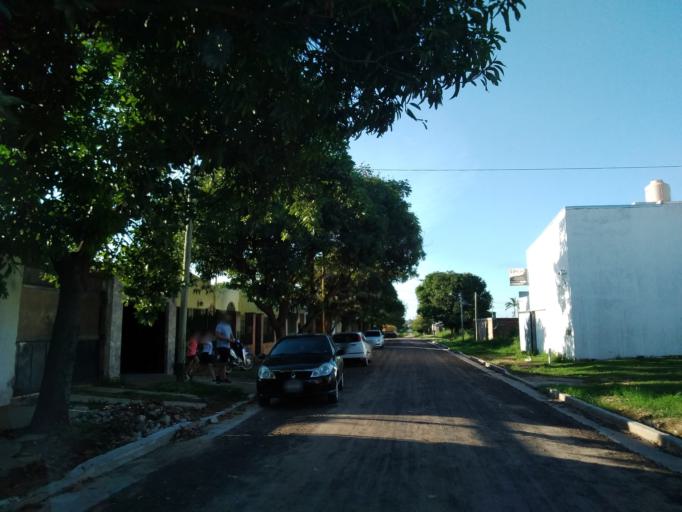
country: AR
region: Corrientes
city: Corrientes
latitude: -27.5055
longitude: -58.8013
